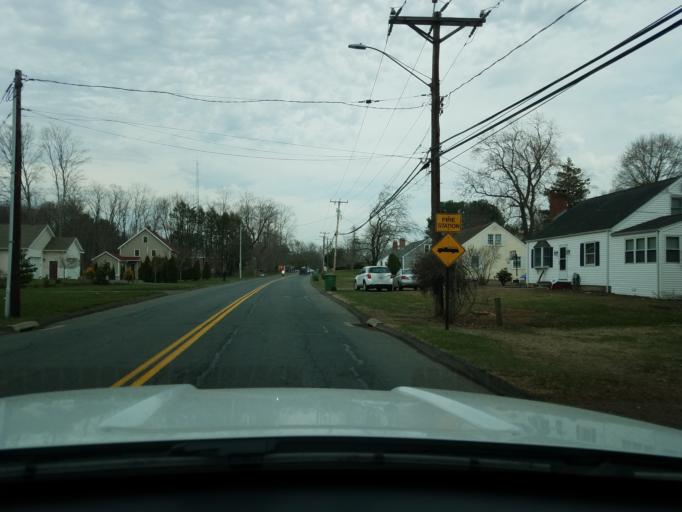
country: US
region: Connecticut
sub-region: Middlesex County
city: Cromwell
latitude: 41.6234
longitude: -72.6713
